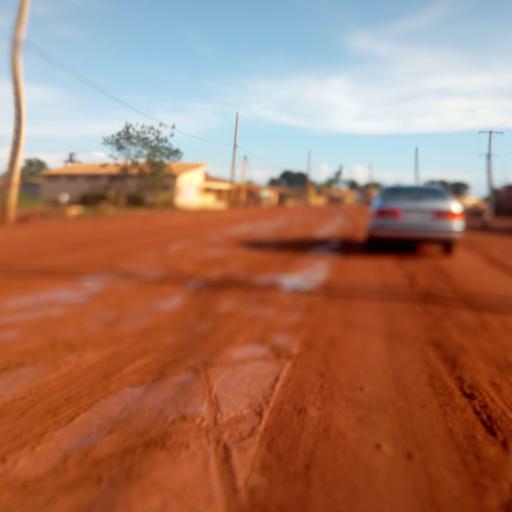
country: BJ
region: Atlantique
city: Hevie
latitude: 6.4122
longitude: 2.2650
